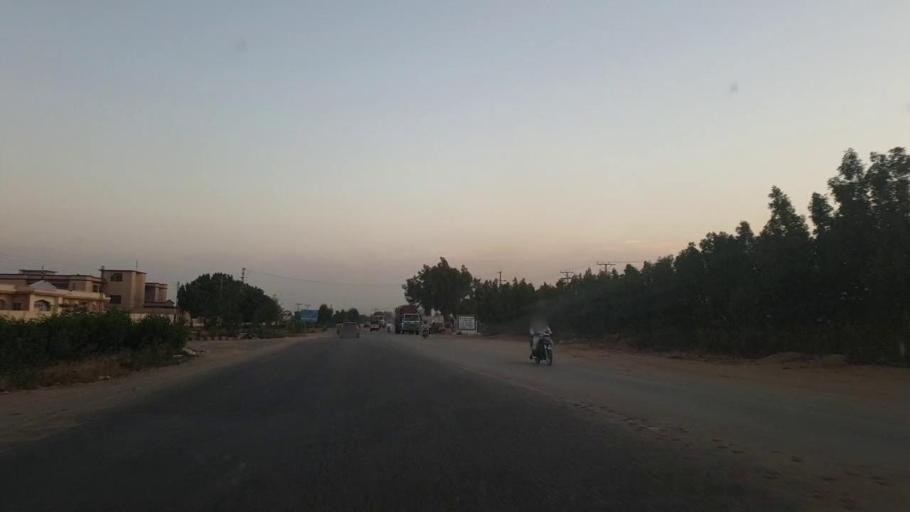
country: PK
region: Sindh
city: Kotri
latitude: 25.3899
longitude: 68.2735
